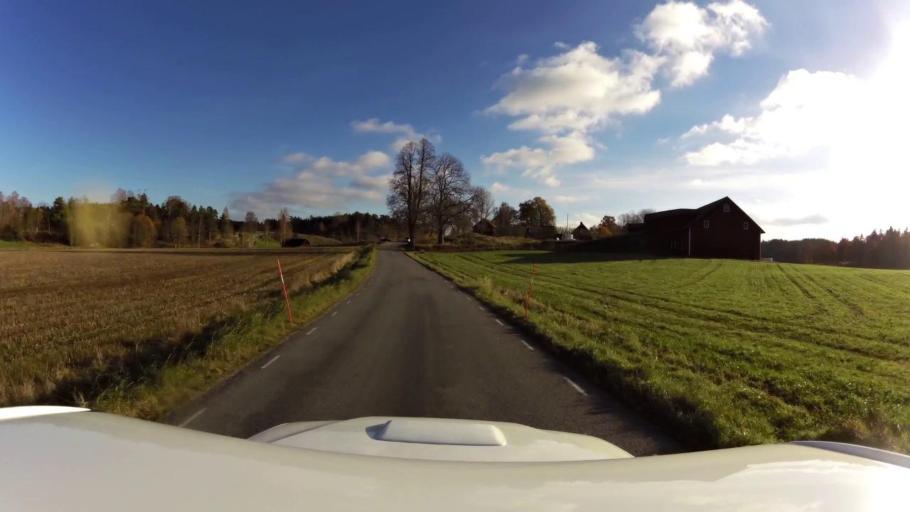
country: SE
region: OEstergoetland
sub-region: Linkopings Kommun
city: Vikingstad
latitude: 58.2570
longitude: 15.4620
